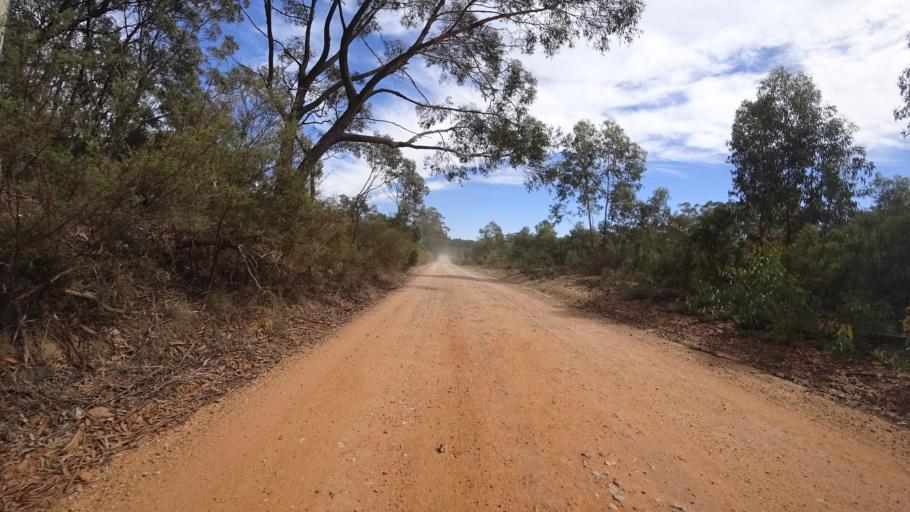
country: AU
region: New South Wales
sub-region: Lithgow
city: Lithgow
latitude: -33.3443
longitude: 150.2549
